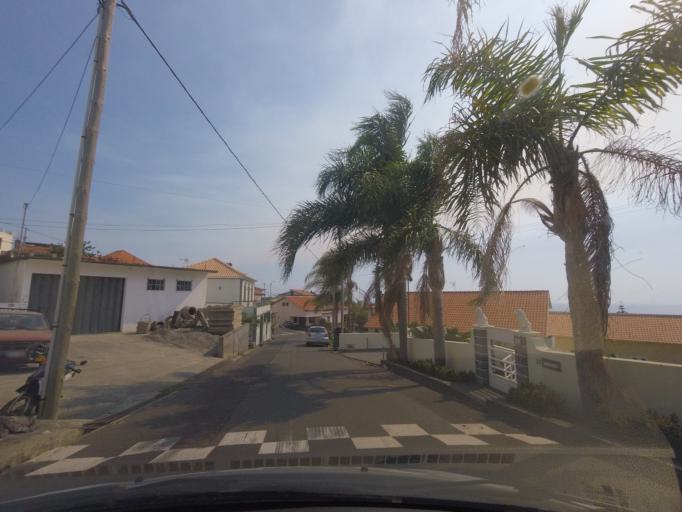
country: PT
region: Madeira
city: Ribeira Brava
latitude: 32.6777
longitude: -17.0657
